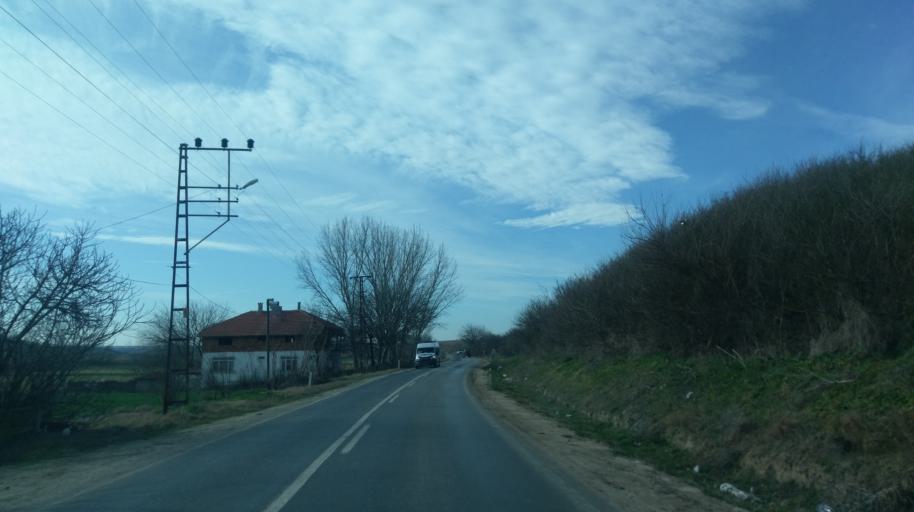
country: TR
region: Kirklareli
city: Pehlivankoy
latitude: 41.3843
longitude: 26.9912
